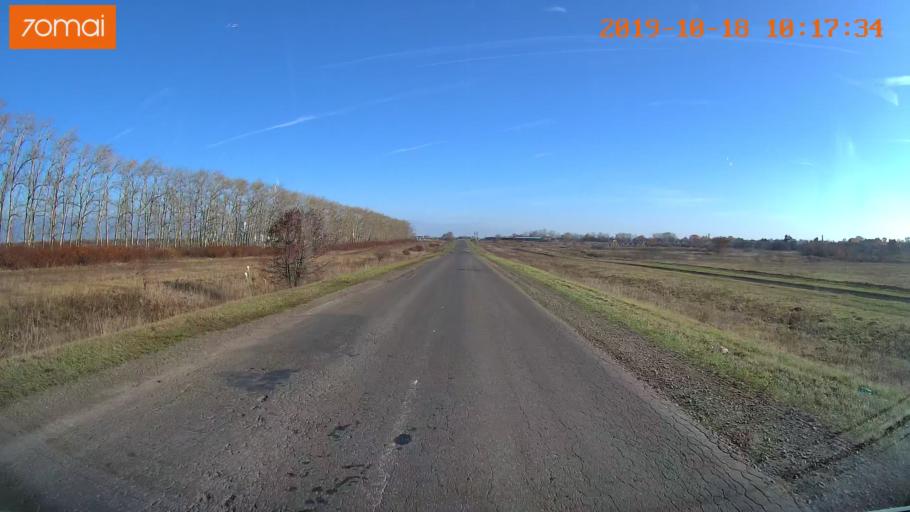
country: RU
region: Tula
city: Kurkino
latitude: 53.4126
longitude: 38.6204
